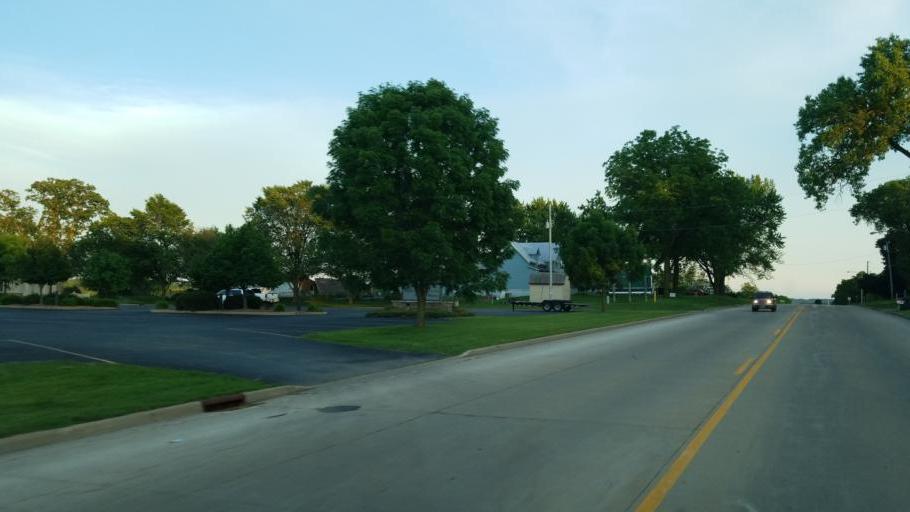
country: US
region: Wisconsin
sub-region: Monroe County
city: Tomah
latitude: 43.9656
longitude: -90.5049
